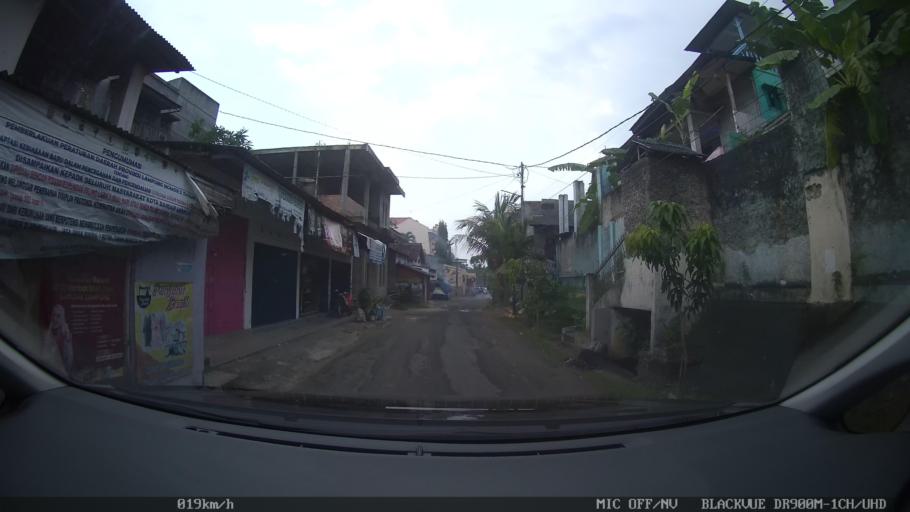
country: ID
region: Lampung
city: Bandarlampung
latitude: -5.4373
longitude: 105.2880
